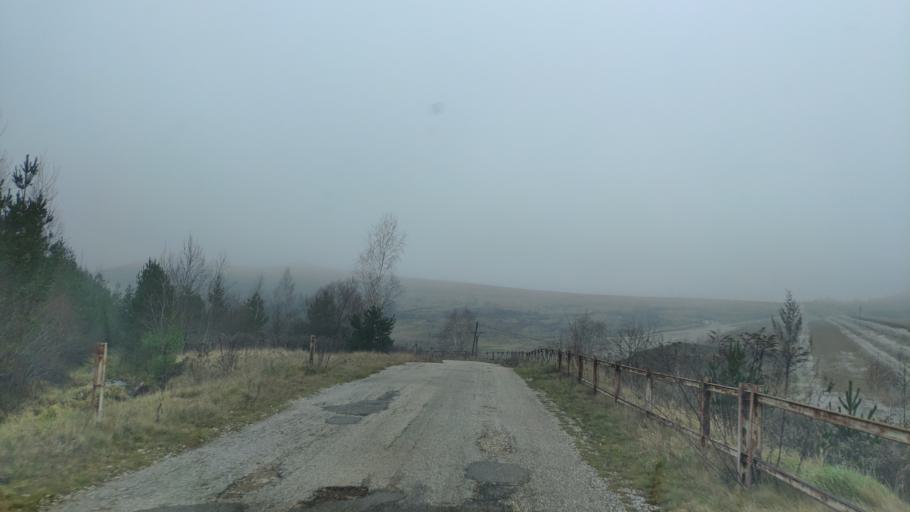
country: SK
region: Banskobystricky
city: Revuca
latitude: 48.6429
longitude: 20.2437
